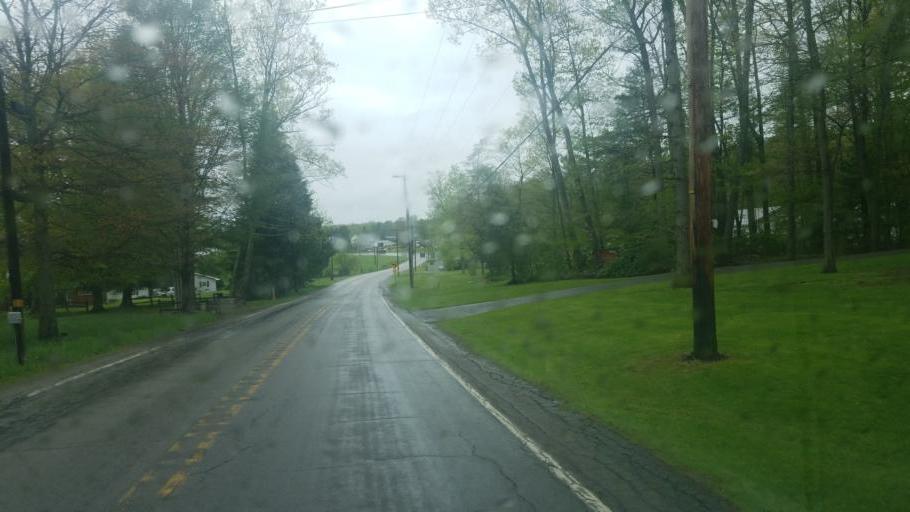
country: US
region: Pennsylvania
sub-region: Clarion County
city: Marianne
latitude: 41.3814
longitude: -79.3175
